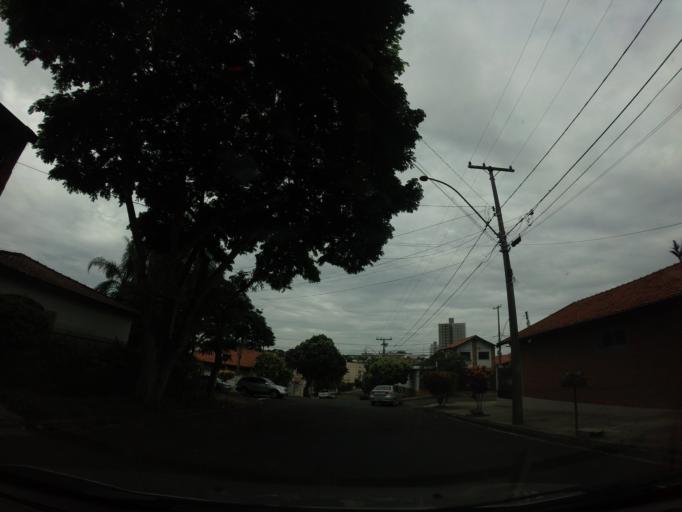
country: BR
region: Sao Paulo
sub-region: Piracicaba
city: Piracicaba
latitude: -22.7086
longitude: -47.6654
